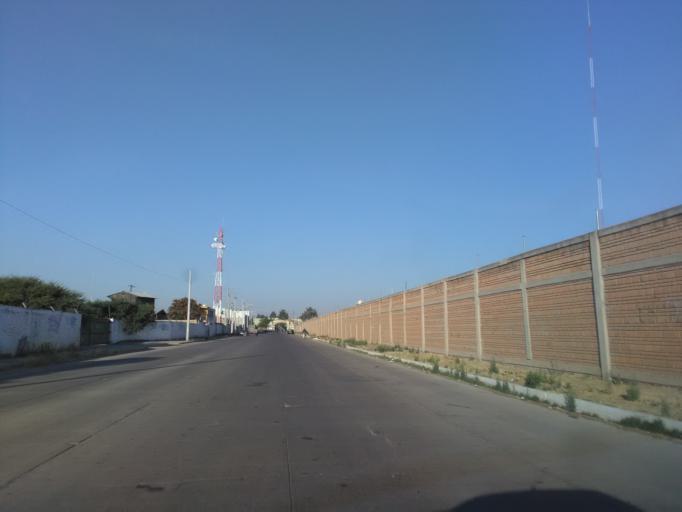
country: MX
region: Durango
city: Victoria de Durango
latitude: 24.0625
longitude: -104.6125
